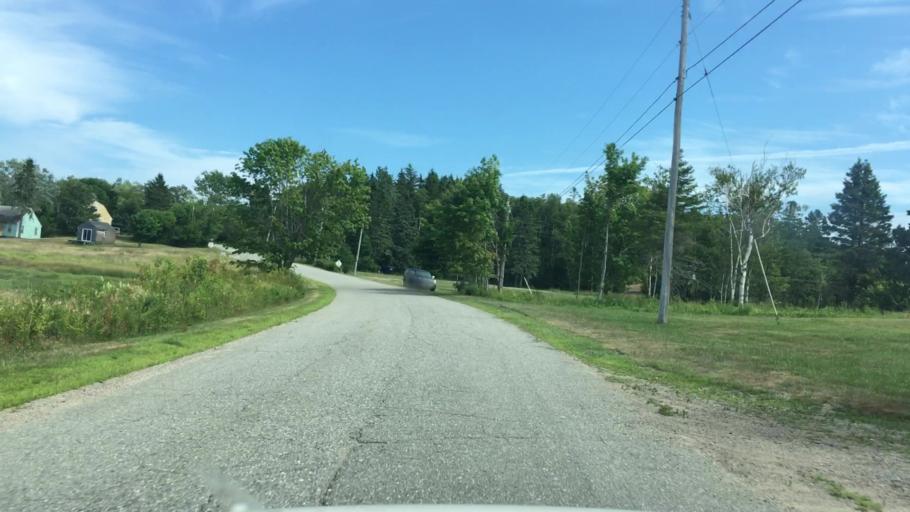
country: US
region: Maine
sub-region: Washington County
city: Eastport
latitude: 44.9279
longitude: -67.0367
